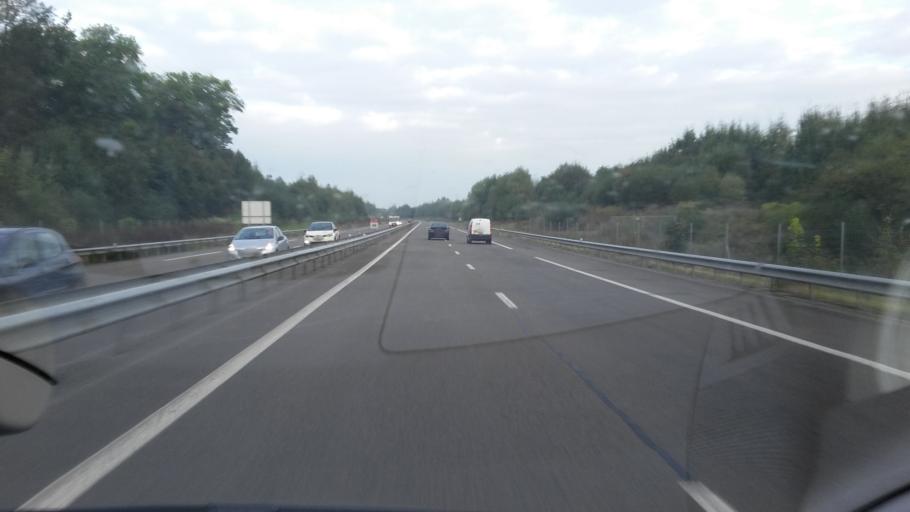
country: FR
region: Champagne-Ardenne
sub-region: Departement des Ardennes
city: La Francheville
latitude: 49.6420
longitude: 4.5978
